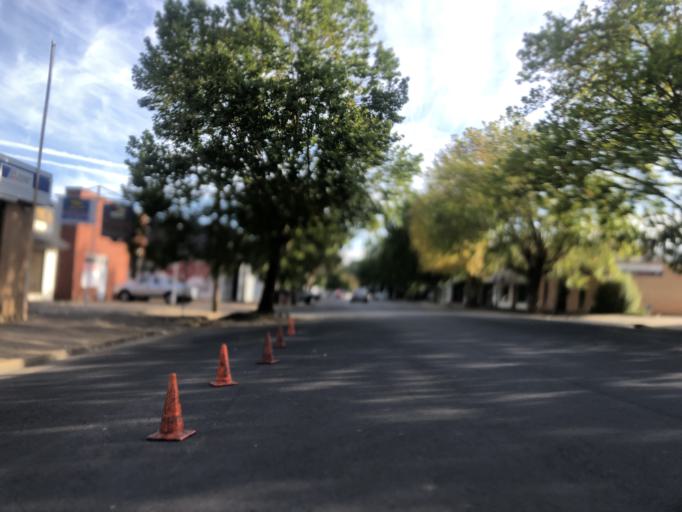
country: AU
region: New South Wales
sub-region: Orange Municipality
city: Orange
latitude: -33.2875
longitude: 149.1003
